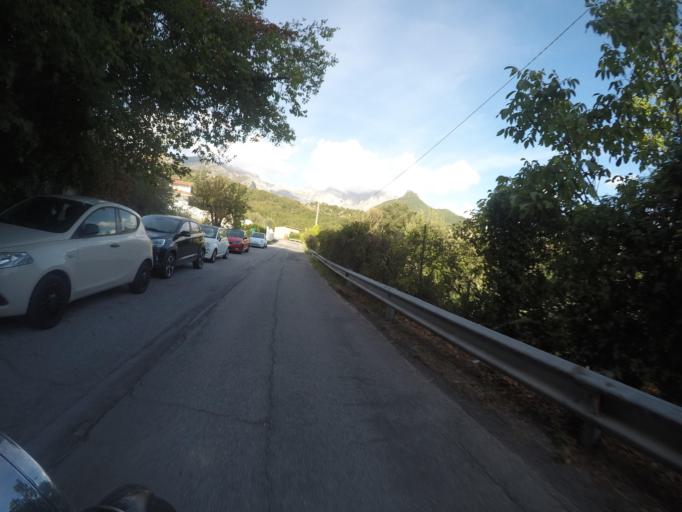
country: IT
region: Tuscany
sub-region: Provincia di Massa-Carrara
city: Carrara
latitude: 44.0870
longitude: 10.0930
